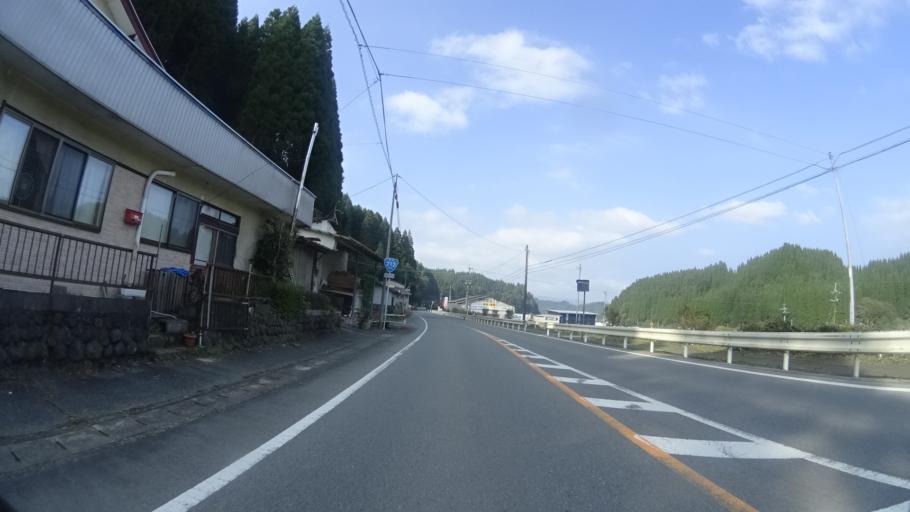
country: JP
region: Kumamoto
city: Aso
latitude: 33.0893
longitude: 131.0677
